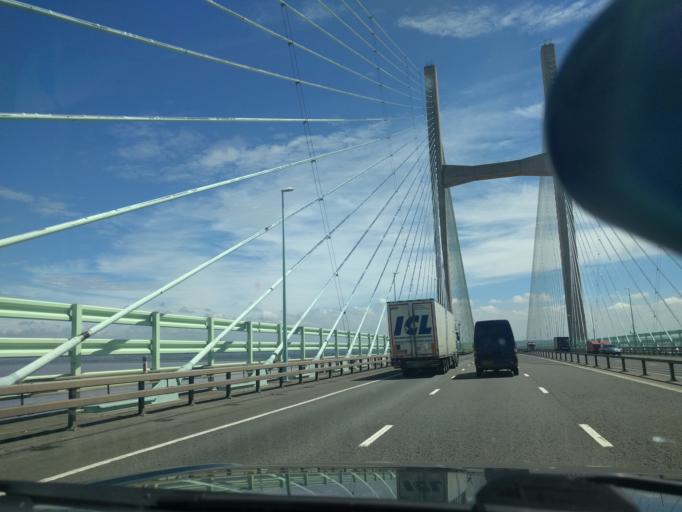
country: GB
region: England
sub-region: South Gloucestershire
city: Severn Beach
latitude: 51.5742
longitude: -2.6994
